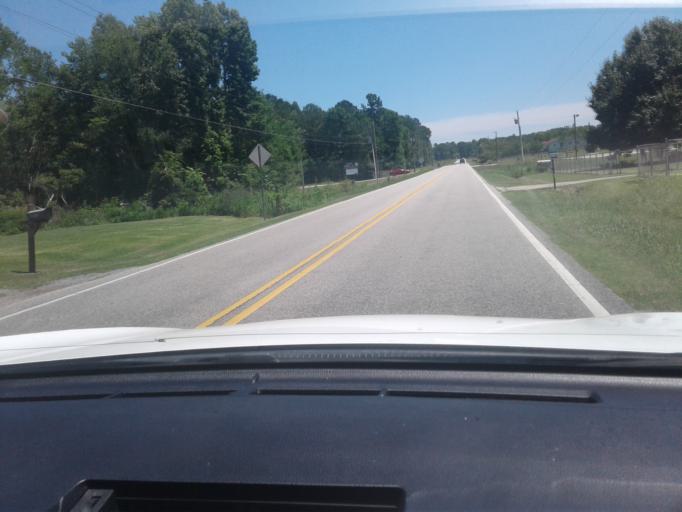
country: US
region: North Carolina
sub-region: Harnett County
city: Erwin
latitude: 35.3155
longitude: -78.7045
